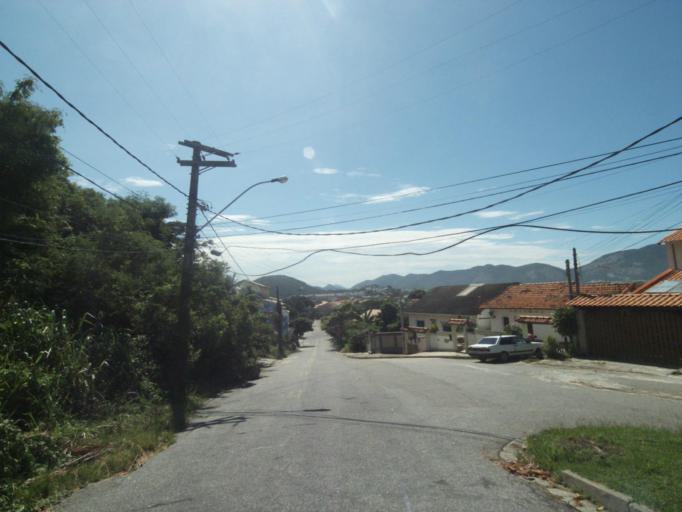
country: BR
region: Rio de Janeiro
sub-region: Niteroi
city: Niteroi
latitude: -22.9561
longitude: -43.0658
